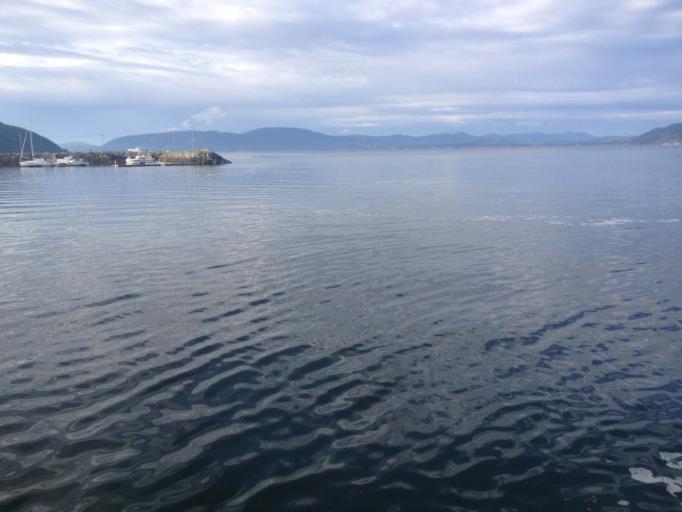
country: NO
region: Sor-Trondelag
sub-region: Agdenes
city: Lensvik
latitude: 63.5052
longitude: 9.8311
